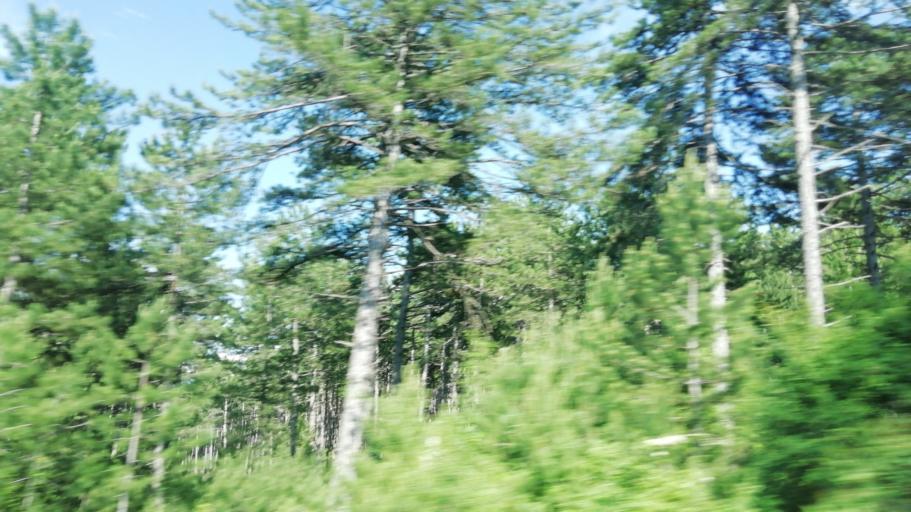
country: TR
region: Karabuk
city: Karabuk
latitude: 41.1124
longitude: 32.6067
